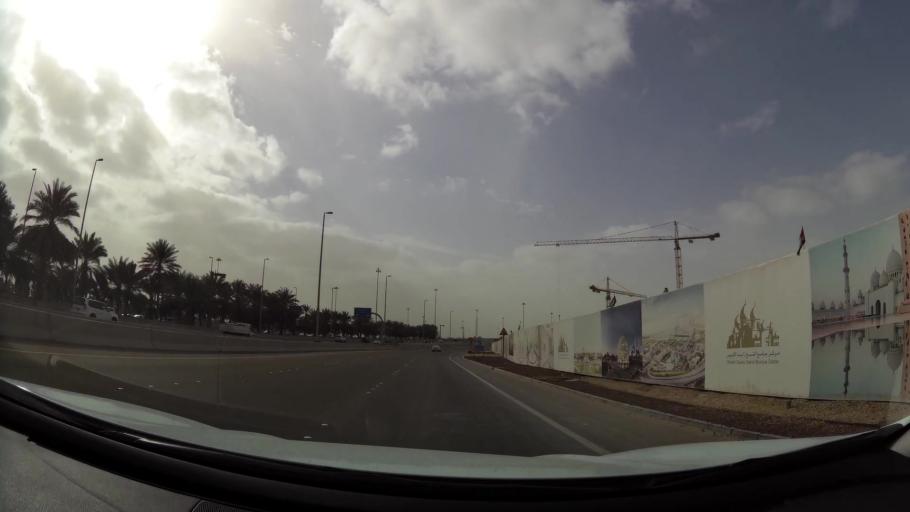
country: AE
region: Abu Dhabi
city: Abu Dhabi
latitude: 24.4104
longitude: 54.4781
